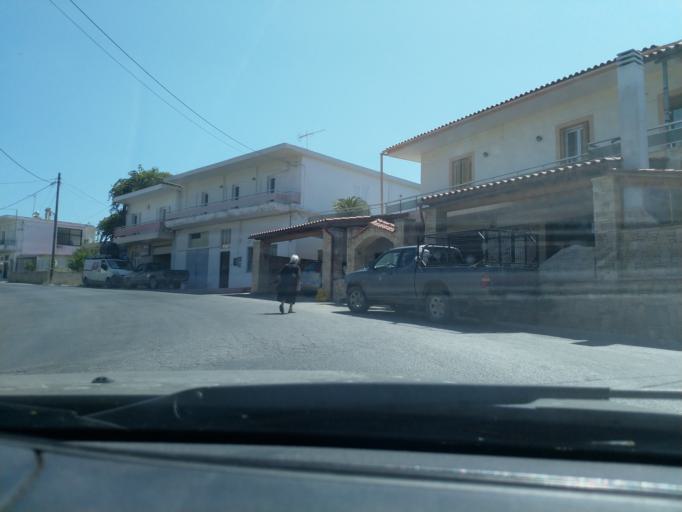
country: GR
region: Crete
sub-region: Nomos Rethymnis
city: Agia Foteini
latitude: 35.2187
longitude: 24.5008
